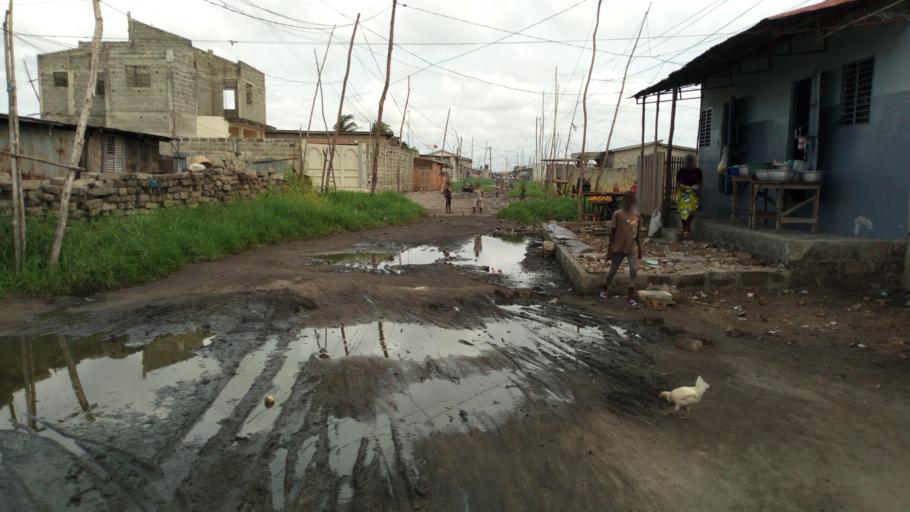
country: BJ
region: Littoral
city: Cotonou
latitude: 6.3899
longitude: 2.4311
